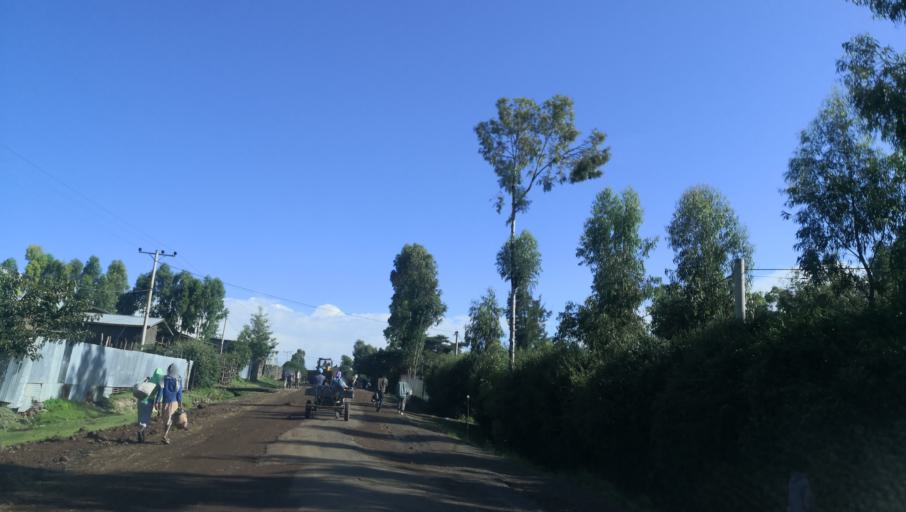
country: ET
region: Oromiya
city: Tulu Bolo
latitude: 8.6502
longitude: 38.2194
